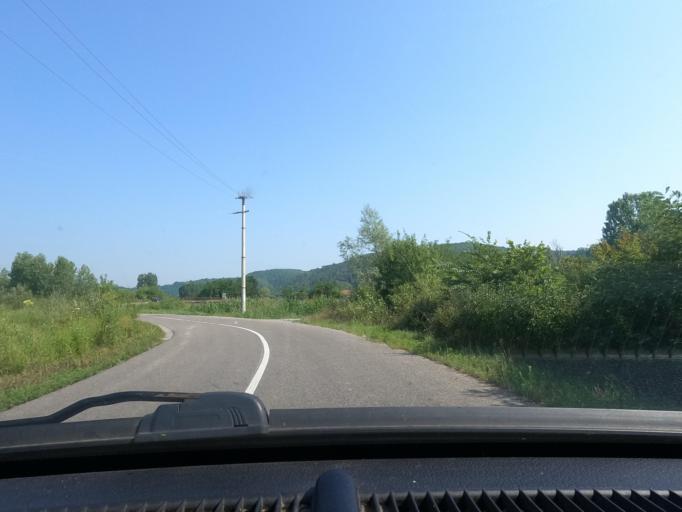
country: RS
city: Kozjak
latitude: 44.5546
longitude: 19.3139
